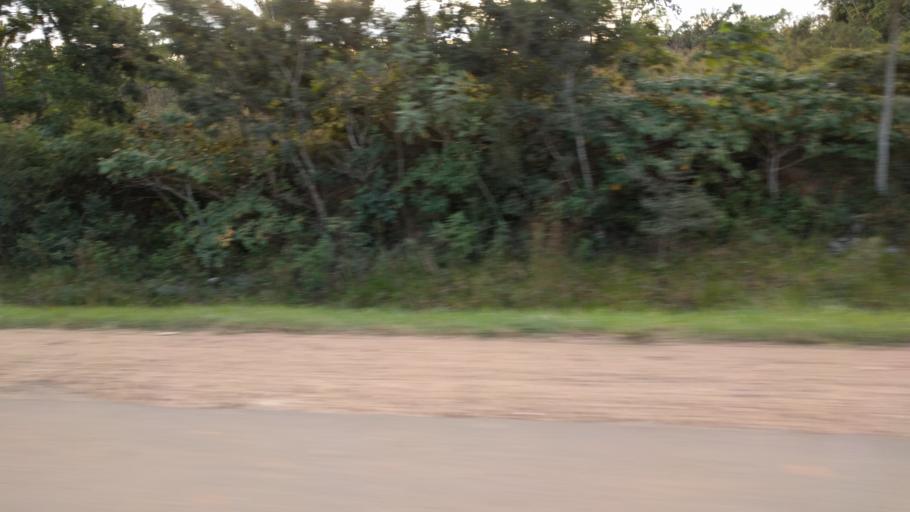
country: BO
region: Santa Cruz
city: Buena Vista
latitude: -17.4396
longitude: -63.6433
